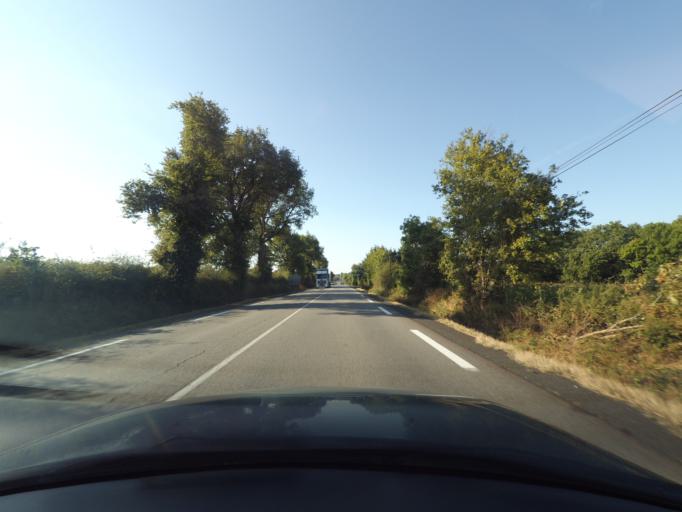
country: FR
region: Poitou-Charentes
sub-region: Departement des Deux-Sevres
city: Chiche
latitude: 46.7505
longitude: -0.3073
